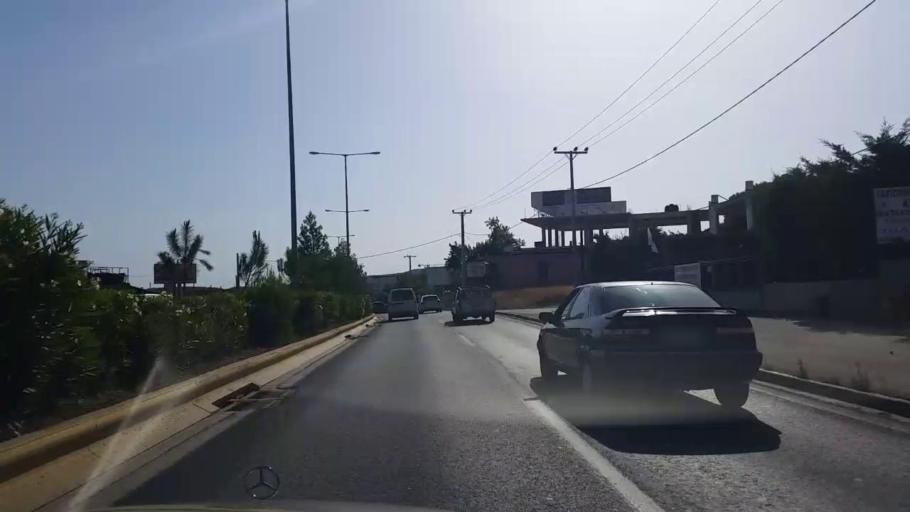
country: GR
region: Attica
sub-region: Nomarchia Anatolikis Attikis
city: Kitsi
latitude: 37.8576
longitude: 23.8367
